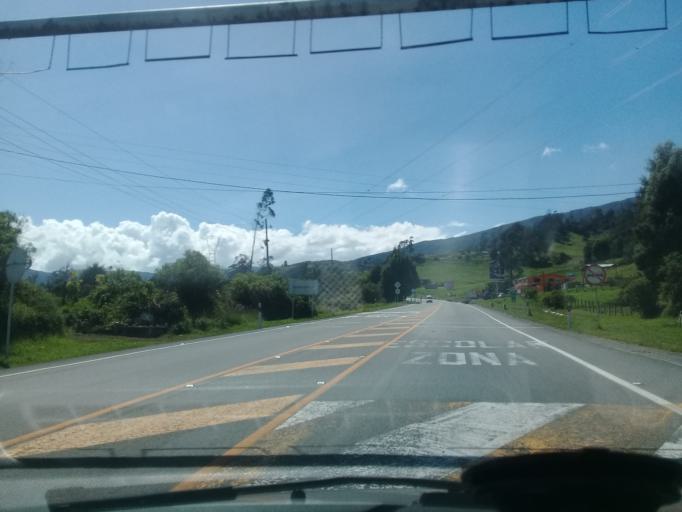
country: CO
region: Cundinamarca
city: Chipaque
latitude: 4.4540
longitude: -74.0504
